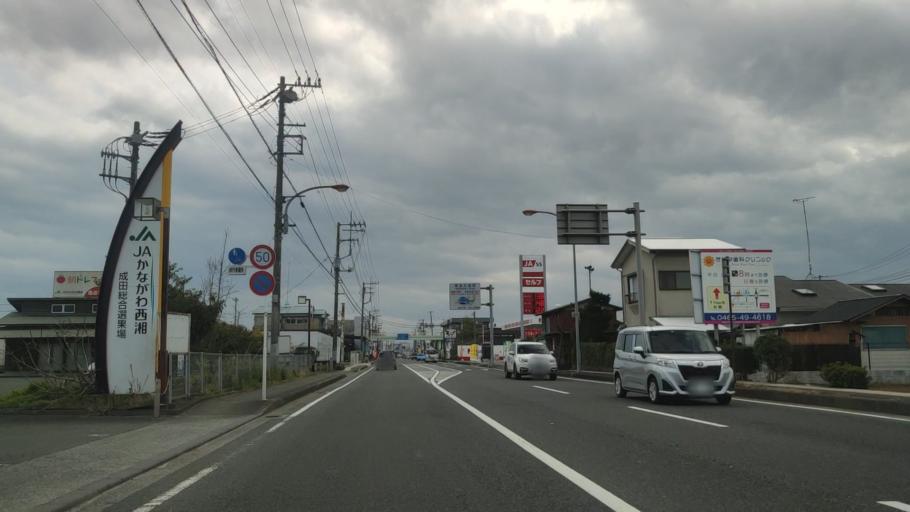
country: JP
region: Kanagawa
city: Odawara
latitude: 35.2974
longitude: 139.1671
